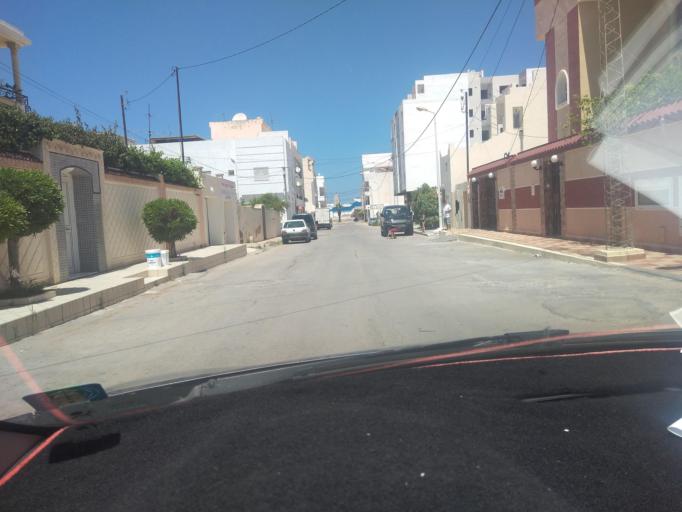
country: TN
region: Susah
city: Hammam Sousse
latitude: 35.8497
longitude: 10.5934
